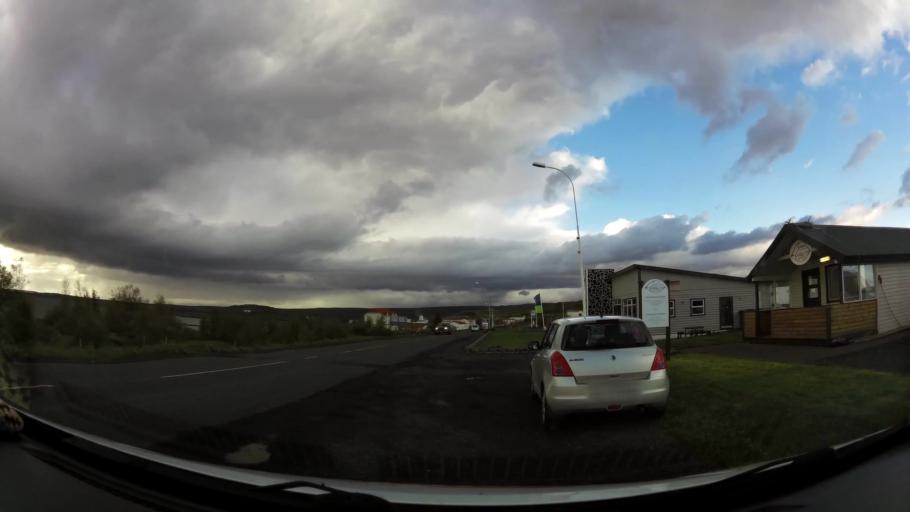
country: IS
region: Northeast
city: Laugar
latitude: 65.6409
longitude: -16.9113
